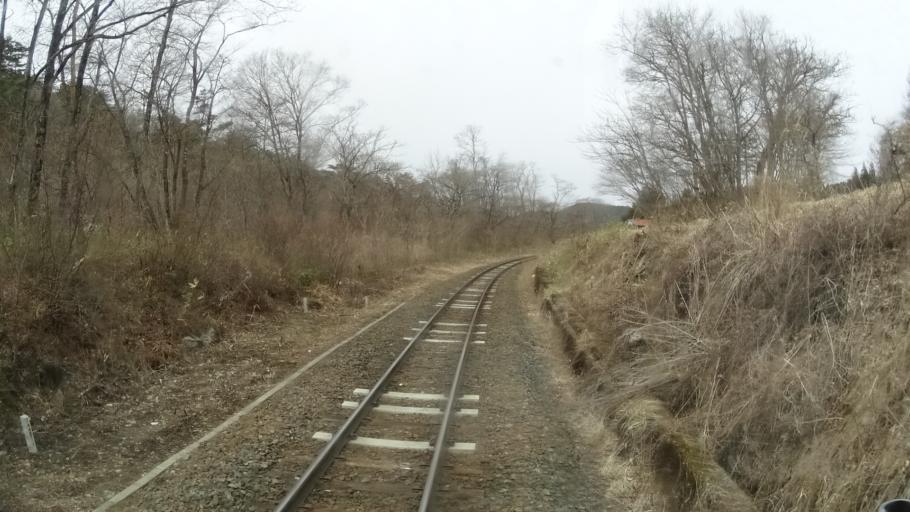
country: JP
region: Iwate
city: Tono
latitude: 39.3270
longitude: 141.3650
